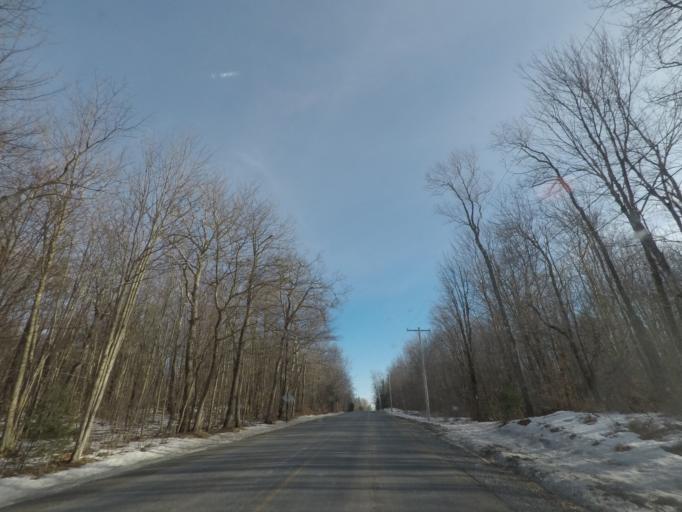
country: US
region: New York
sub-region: Rensselaer County
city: Poestenkill
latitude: 42.7493
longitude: -73.4154
